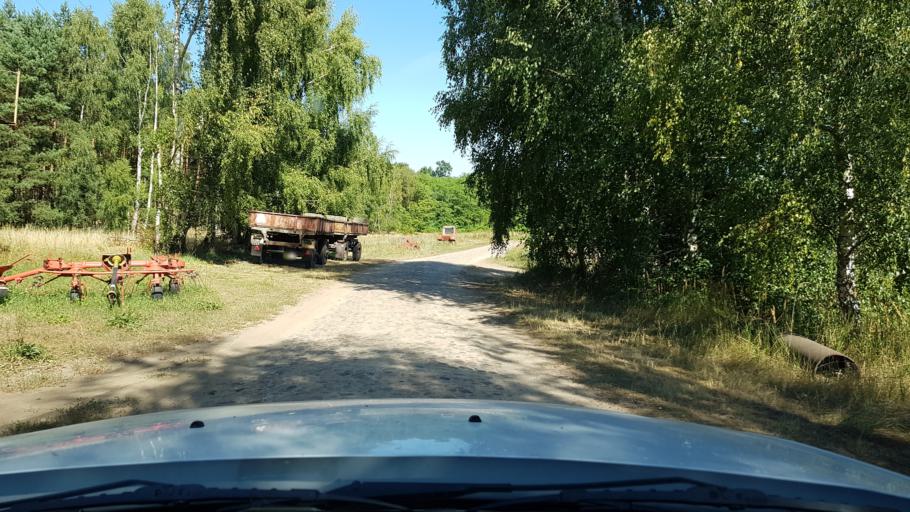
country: PL
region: West Pomeranian Voivodeship
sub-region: Powiat gryfinski
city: Cedynia
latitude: 52.8371
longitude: 14.2071
